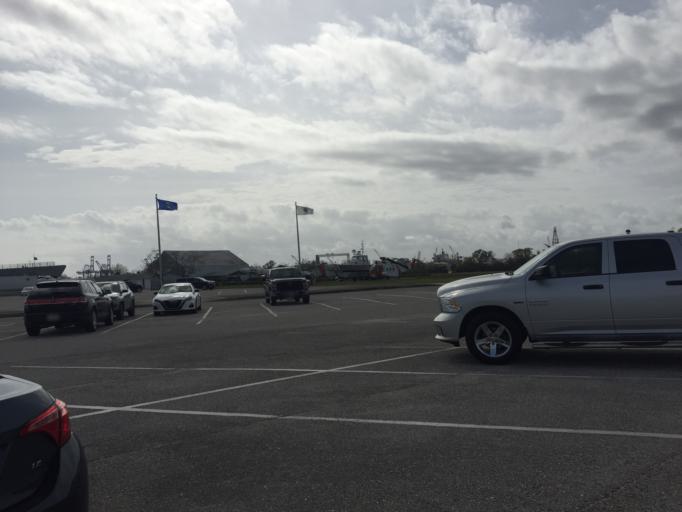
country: US
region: Alabama
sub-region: Mobile County
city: Mobile
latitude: 30.6828
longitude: -88.0158
